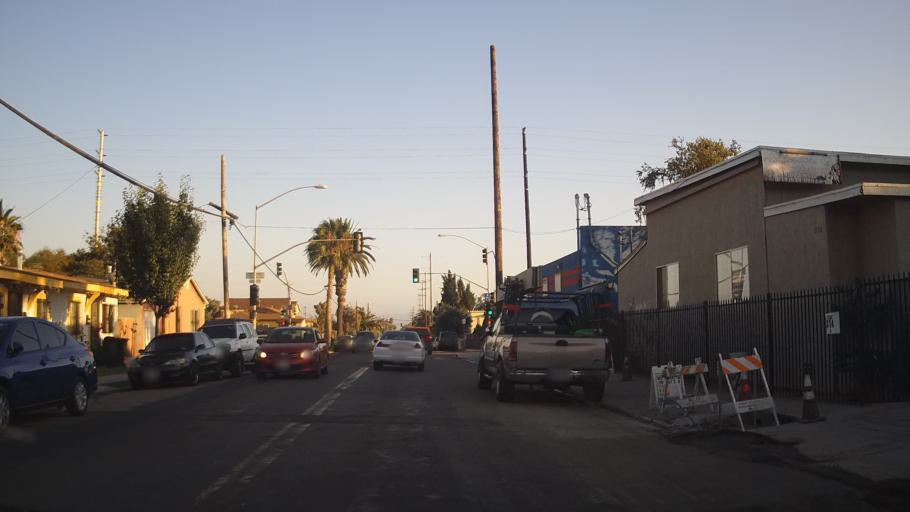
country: US
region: California
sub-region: San Diego County
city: San Diego
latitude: 32.7091
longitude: -117.1339
